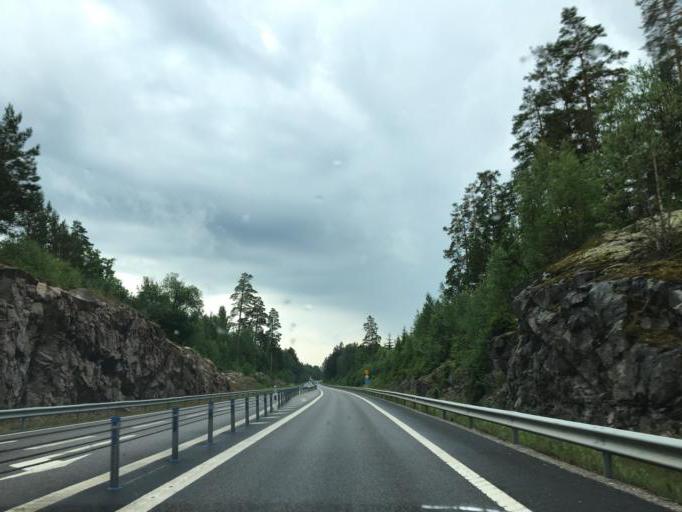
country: SE
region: OEstergoetland
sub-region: Norrkopings Kommun
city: Jursla
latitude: 58.7962
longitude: 16.1551
